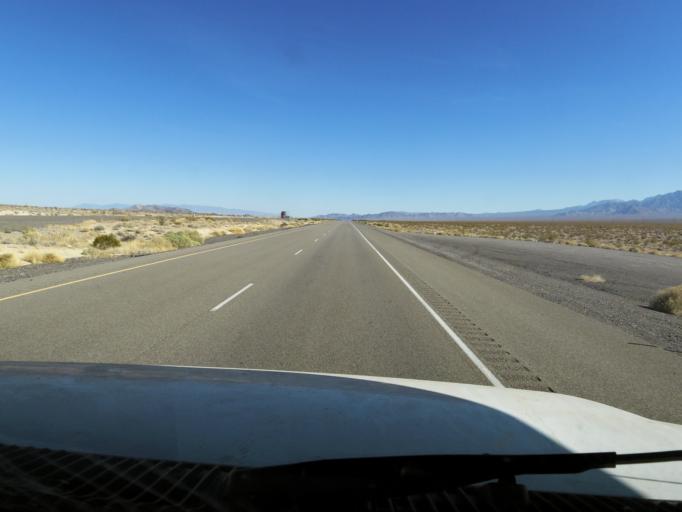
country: US
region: Nevada
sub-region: Nye County
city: Pahrump
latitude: 36.5982
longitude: -115.9573
